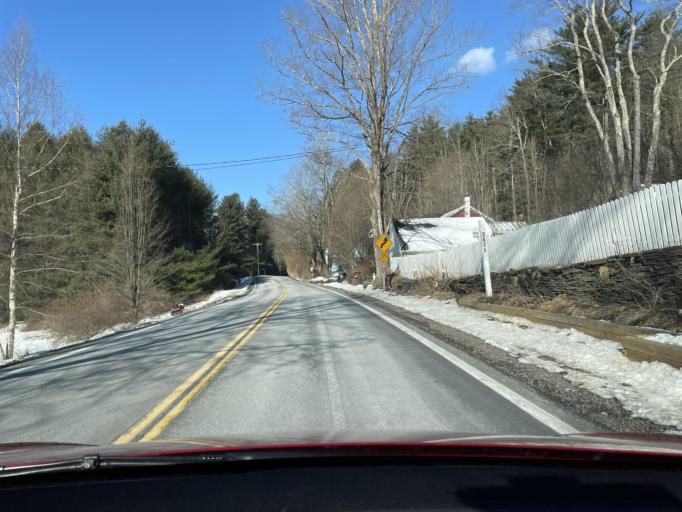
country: US
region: New York
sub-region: Ulster County
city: Woodstock
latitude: 42.0773
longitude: -74.2102
